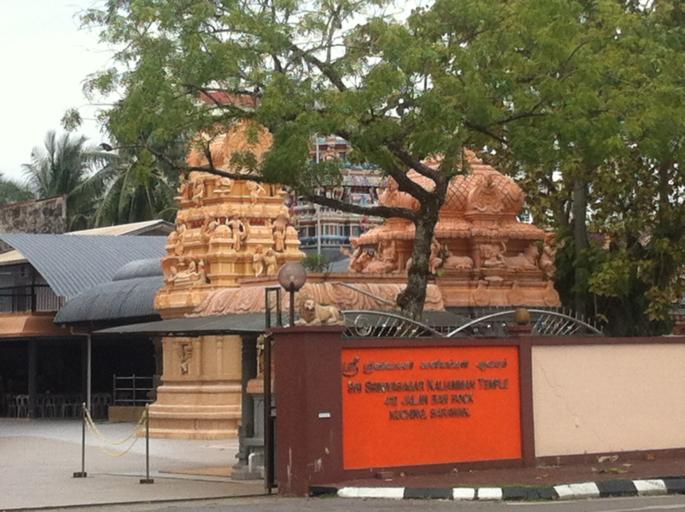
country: MY
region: Sarawak
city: Kuching
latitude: 1.5527
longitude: 110.3530
